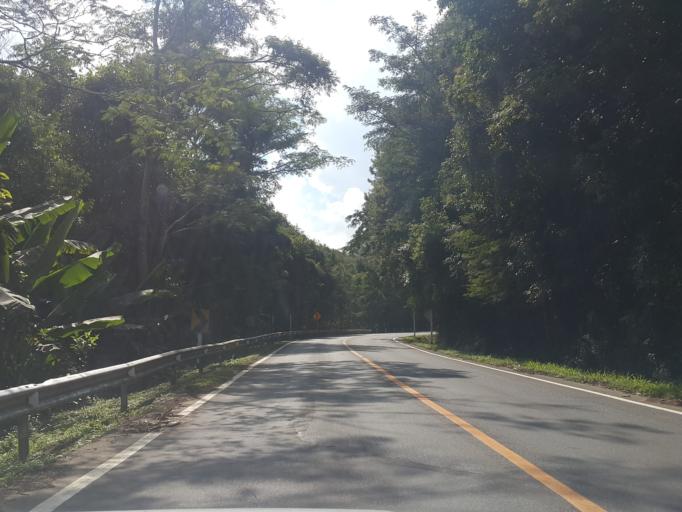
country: TH
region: Chiang Mai
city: Mae Chaem
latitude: 18.5467
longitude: 98.5385
